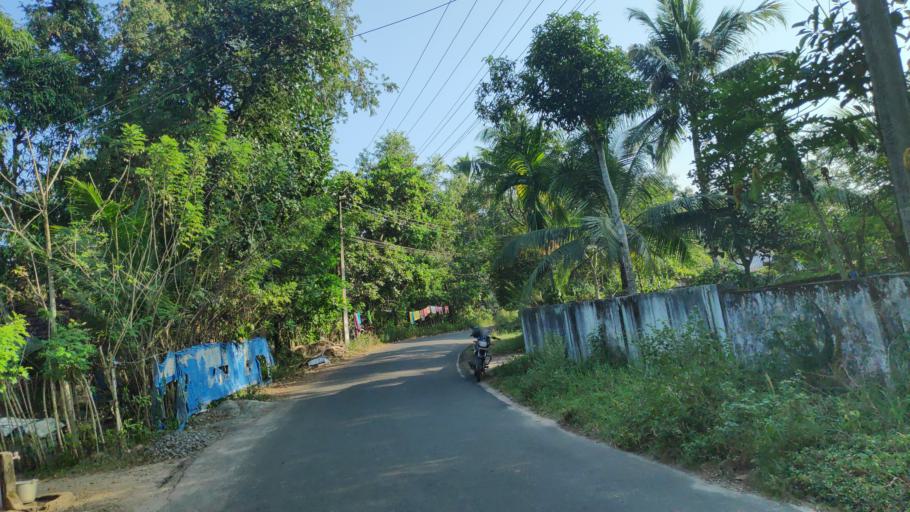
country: IN
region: Kerala
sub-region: Alappuzha
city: Alleppey
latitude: 9.5841
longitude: 76.3414
